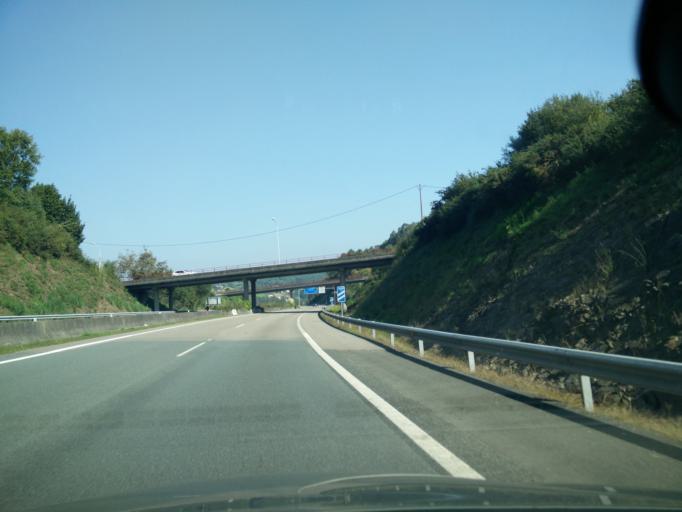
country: ES
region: Galicia
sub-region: Provincia da Coruna
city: Mino
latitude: 43.3456
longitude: -8.2024
